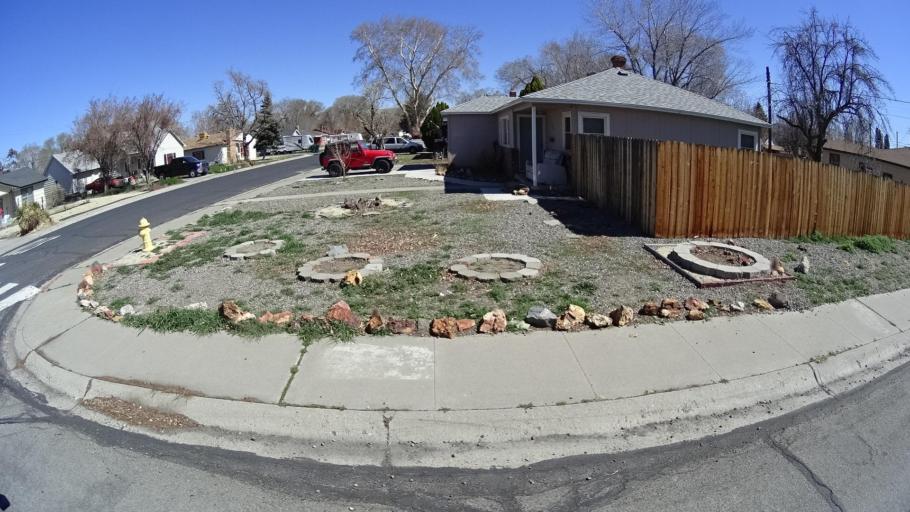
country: US
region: Nevada
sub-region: Washoe County
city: Sparks
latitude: 39.5428
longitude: -119.7484
